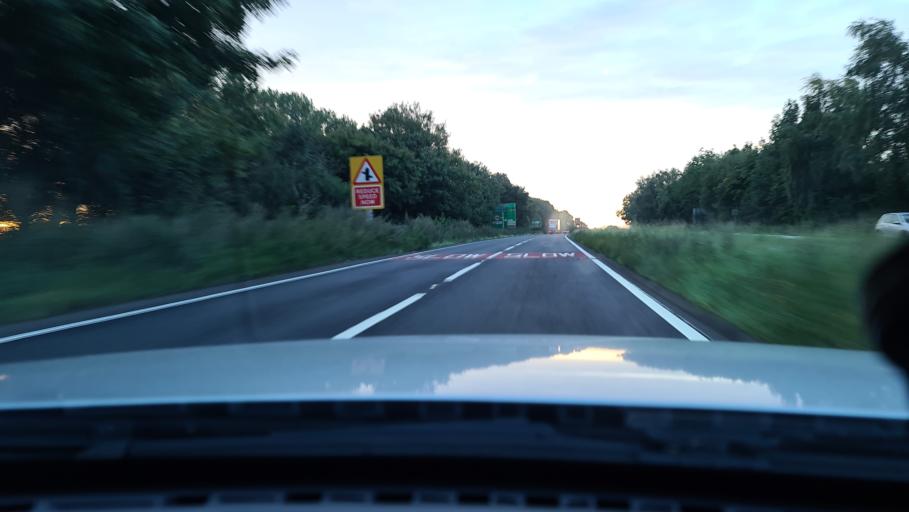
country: GB
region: England
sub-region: Leicestershire
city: Sapcote
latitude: 52.4959
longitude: -1.3097
